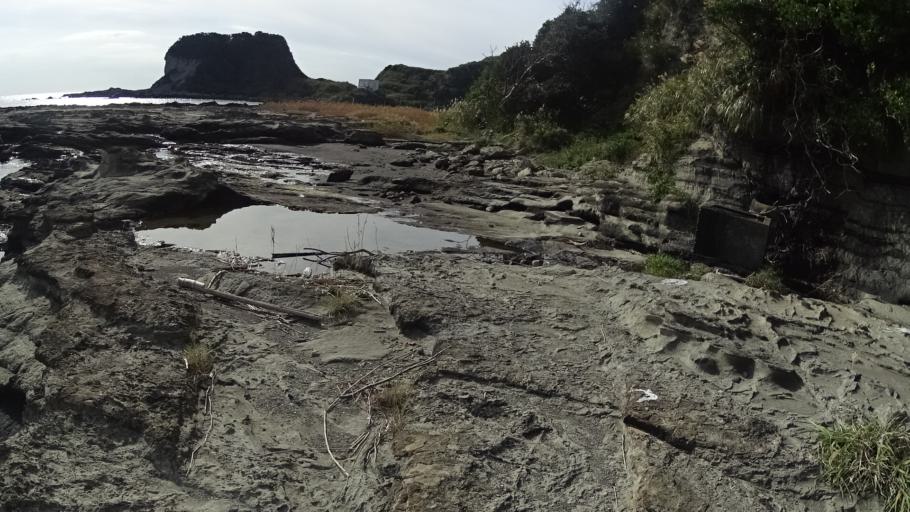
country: JP
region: Kanagawa
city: Miura
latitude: 35.1421
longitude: 139.6727
